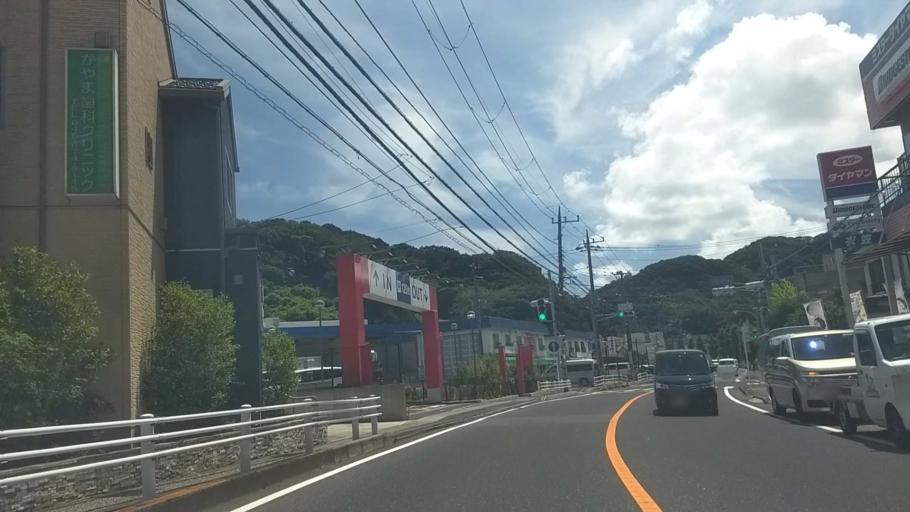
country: JP
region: Kanagawa
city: Yokosuka
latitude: 35.2521
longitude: 139.6659
